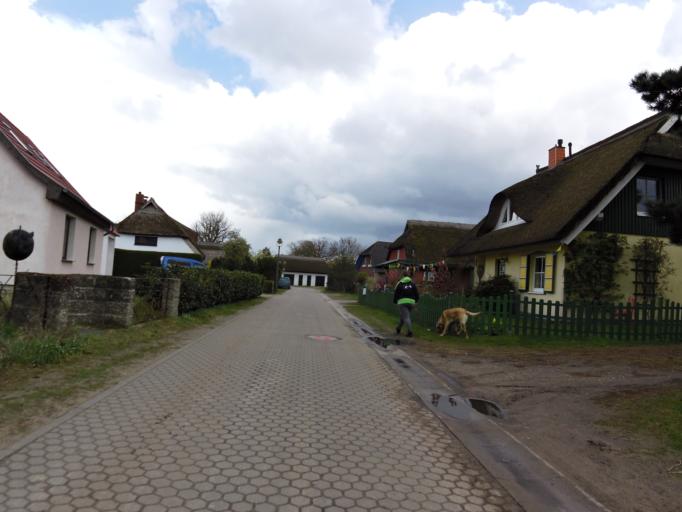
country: DE
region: Mecklenburg-Vorpommern
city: Born
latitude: 54.3799
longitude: 12.5180
